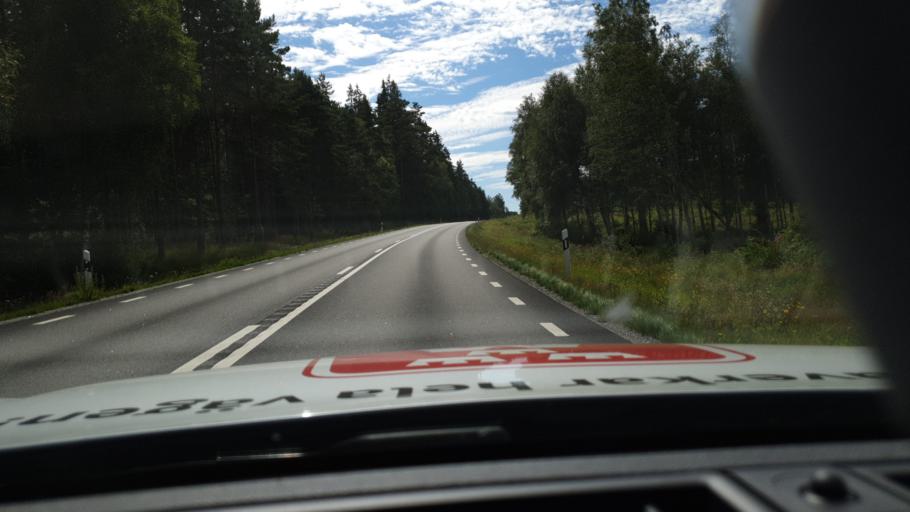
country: SE
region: Joenkoeping
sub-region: Savsjo Kommun
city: Stockaryd
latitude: 57.3010
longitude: 14.5207
